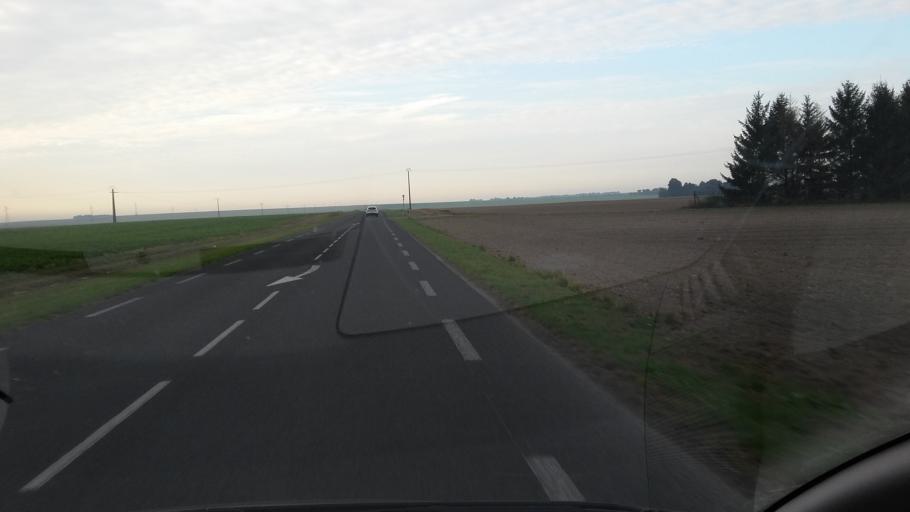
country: FR
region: Champagne-Ardenne
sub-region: Departement de la Marne
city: Fere-Champenoise
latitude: 48.8093
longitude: 3.9927
